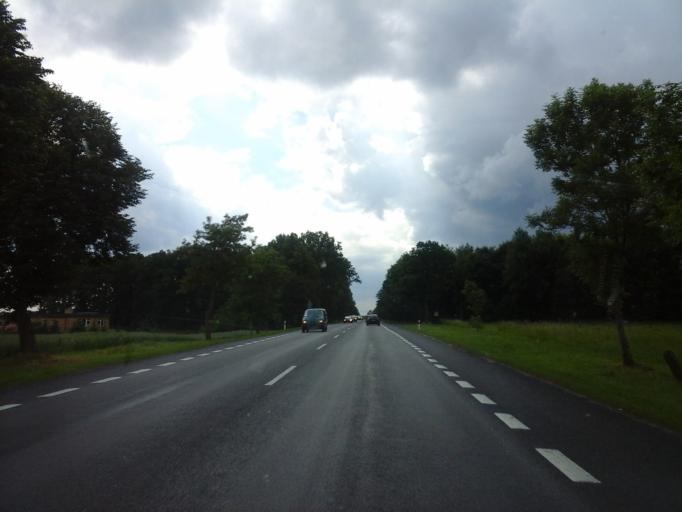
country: PL
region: West Pomeranian Voivodeship
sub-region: Powiat bialogardzki
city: Karlino
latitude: 54.0545
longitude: 15.9186
